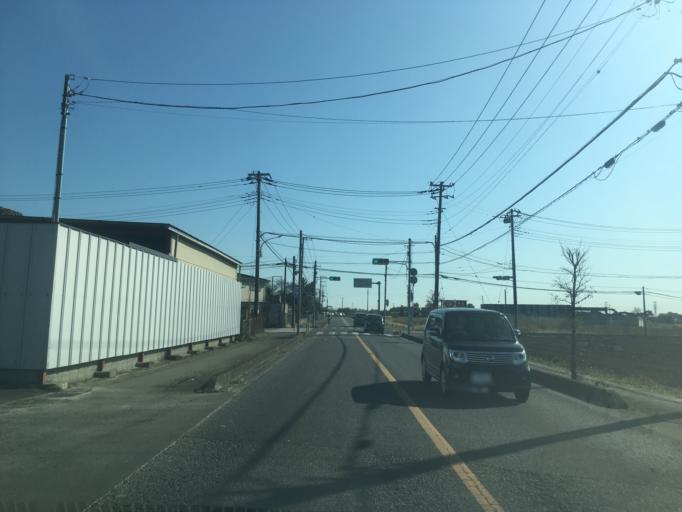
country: JP
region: Saitama
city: Kawagoe
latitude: 35.9450
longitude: 139.4622
